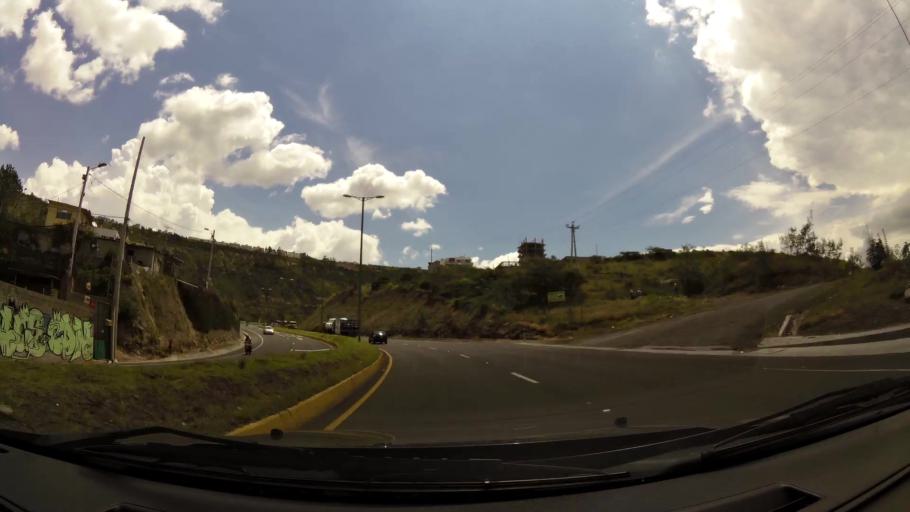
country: EC
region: Pichincha
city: Quito
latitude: -0.1011
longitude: -78.4123
